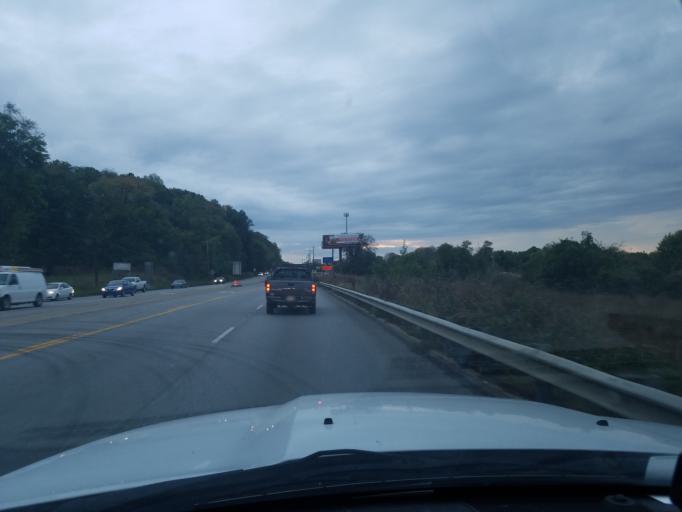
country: US
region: Kentucky
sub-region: Henderson County
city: Henderson
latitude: 37.8873
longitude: -87.5589
